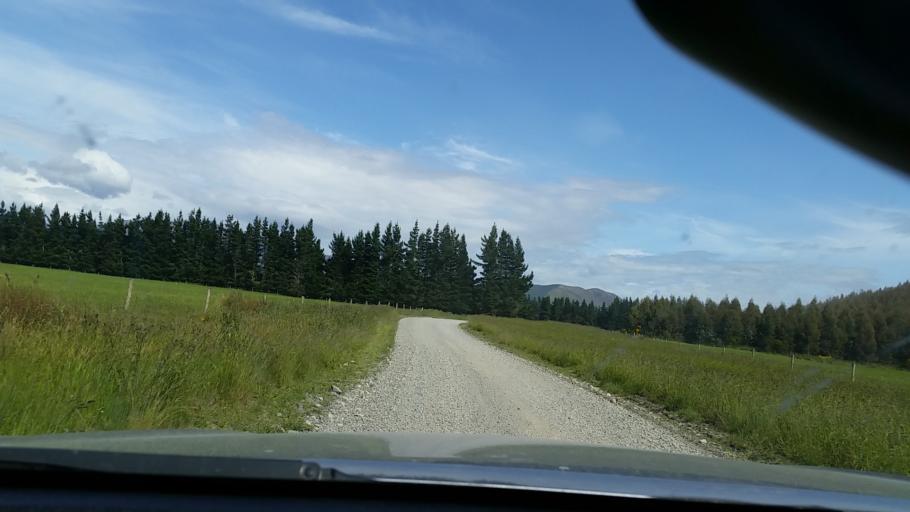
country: NZ
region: Southland
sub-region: Southland District
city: Te Anau
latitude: -45.6188
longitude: 168.1775
